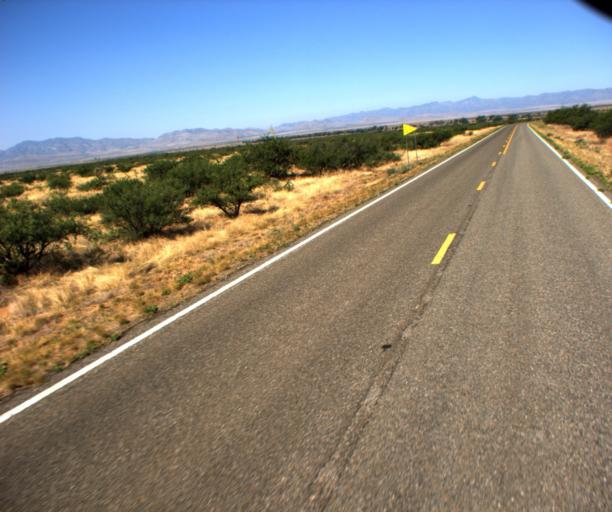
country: US
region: Arizona
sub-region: Graham County
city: Swift Trail Junction
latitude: 32.5828
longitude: -109.9457
